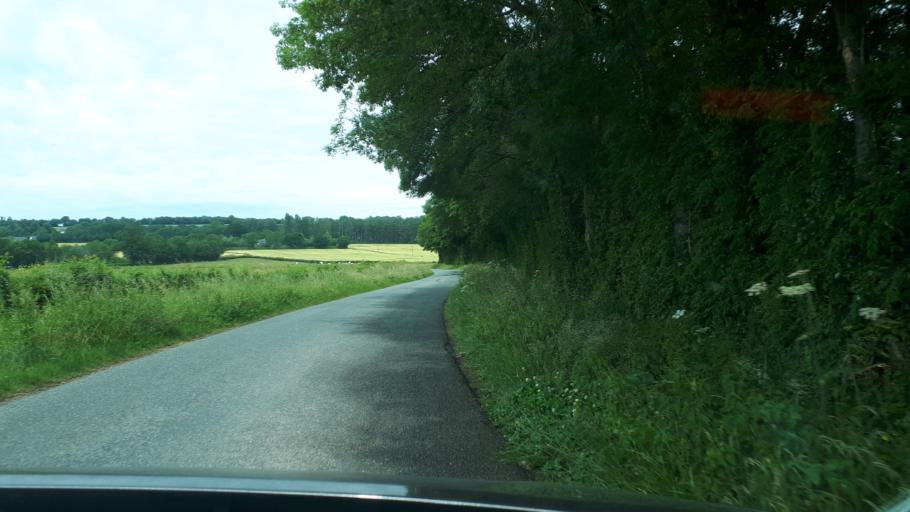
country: FR
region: Centre
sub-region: Departement du Cher
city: Henrichemont
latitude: 47.4111
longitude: 2.6280
